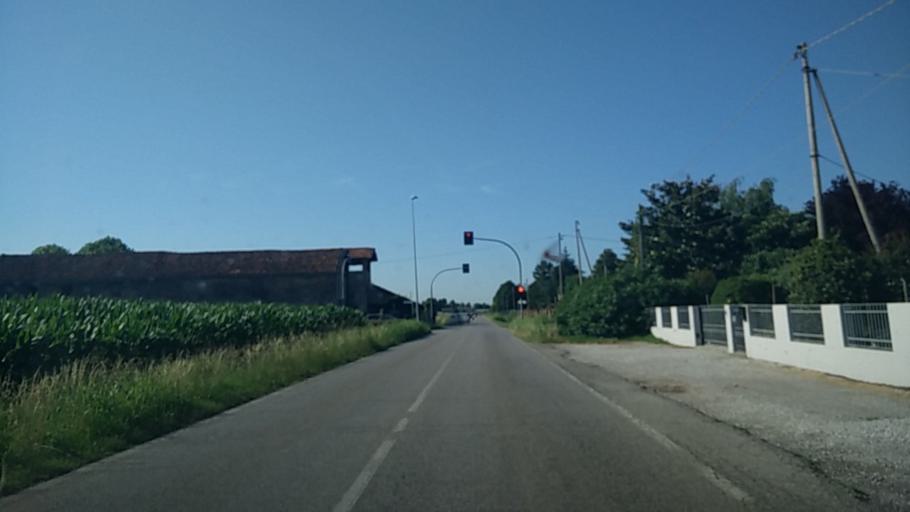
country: IT
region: Veneto
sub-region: Provincia di Venezia
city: Dolo
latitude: 45.4126
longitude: 12.0820
